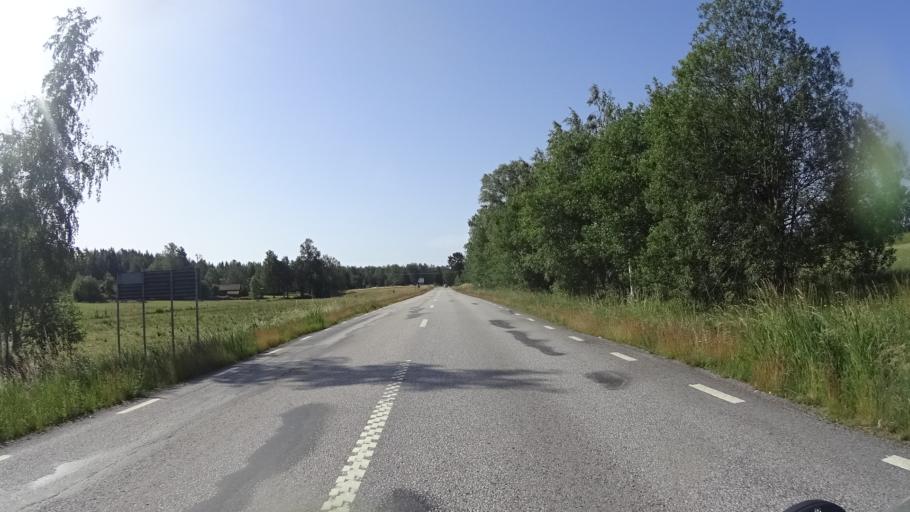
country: SE
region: OEstergoetland
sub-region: Atvidabergs Kommun
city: Atvidaberg
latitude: 58.1193
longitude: 16.0962
